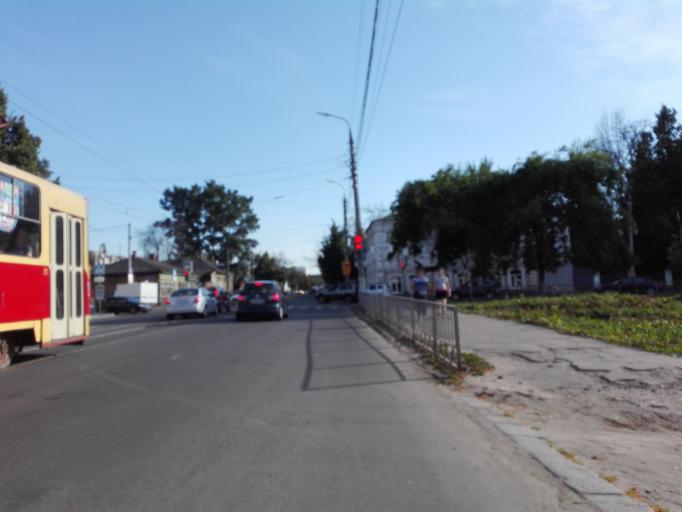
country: RU
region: Orjol
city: Orel
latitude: 52.9586
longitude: 36.0613
